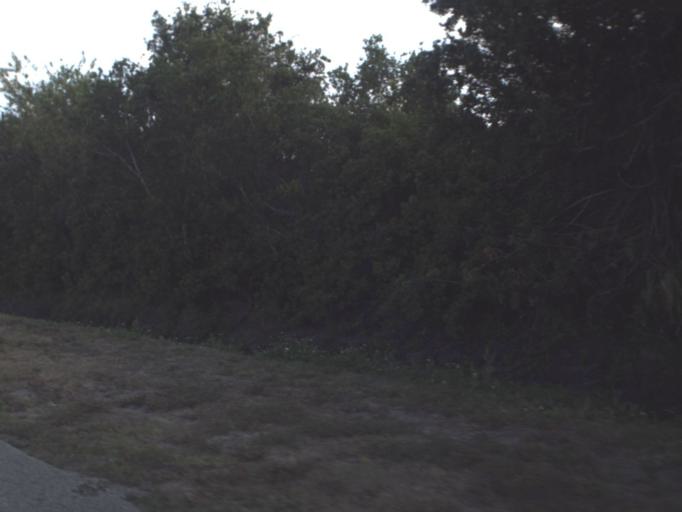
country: US
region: Florida
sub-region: Brevard County
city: Rockledge
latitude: 28.2985
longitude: -80.7017
